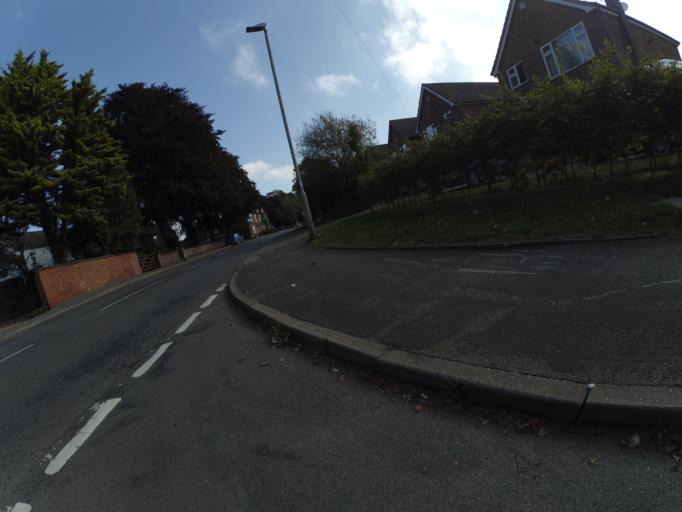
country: GB
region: England
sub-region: Warwickshire
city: Rugby
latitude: 52.3827
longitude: -1.2226
